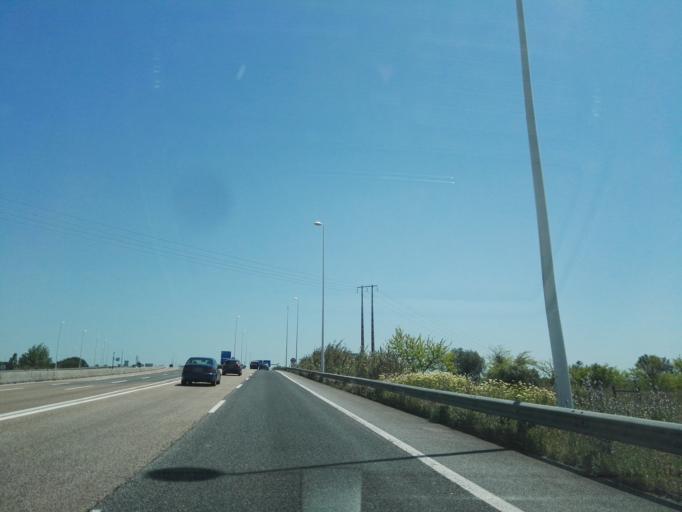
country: PT
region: Setubal
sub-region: Montijo
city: Montijo
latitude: 38.7171
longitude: -8.9486
